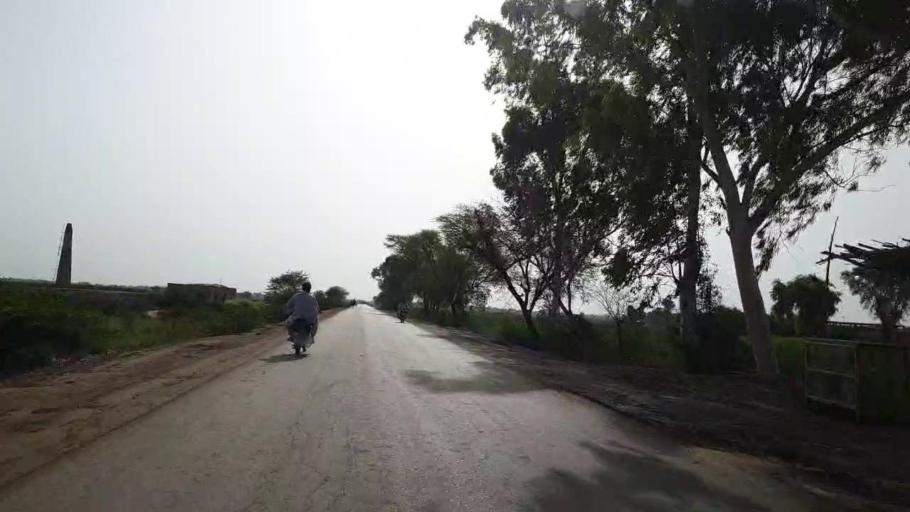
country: PK
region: Sindh
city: Nawabshah
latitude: 26.2617
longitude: 68.4914
